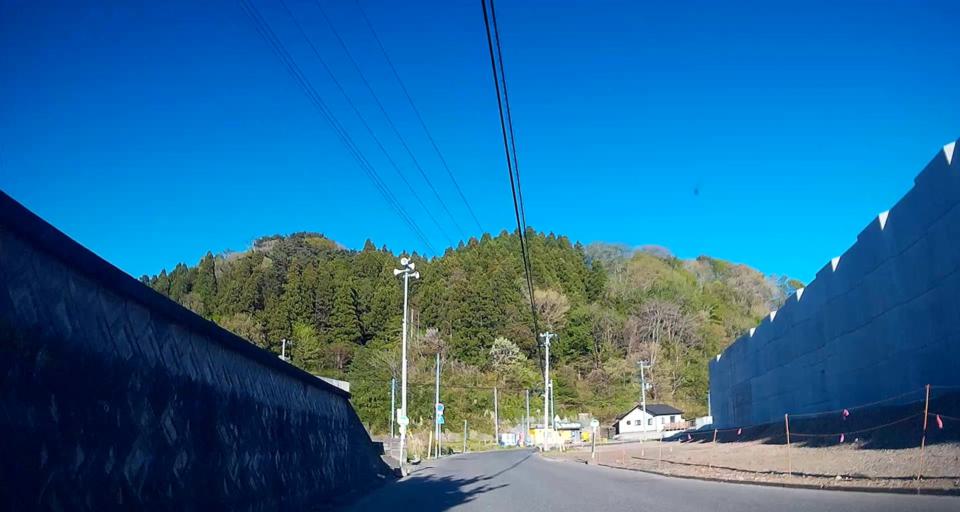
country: JP
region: Iwate
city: Miyako
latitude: 39.6472
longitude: 141.9706
